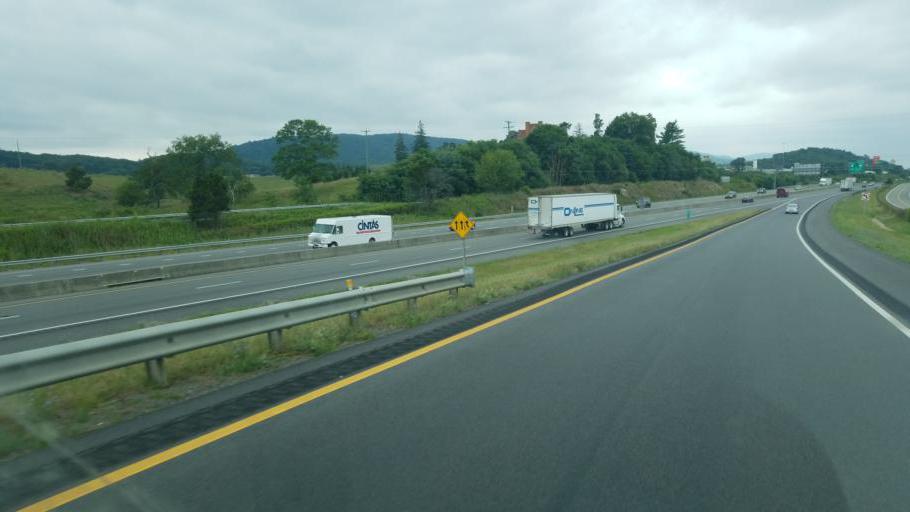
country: US
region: Virginia
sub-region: Wythe County
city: Wytheville
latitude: 36.9479
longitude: -80.9339
